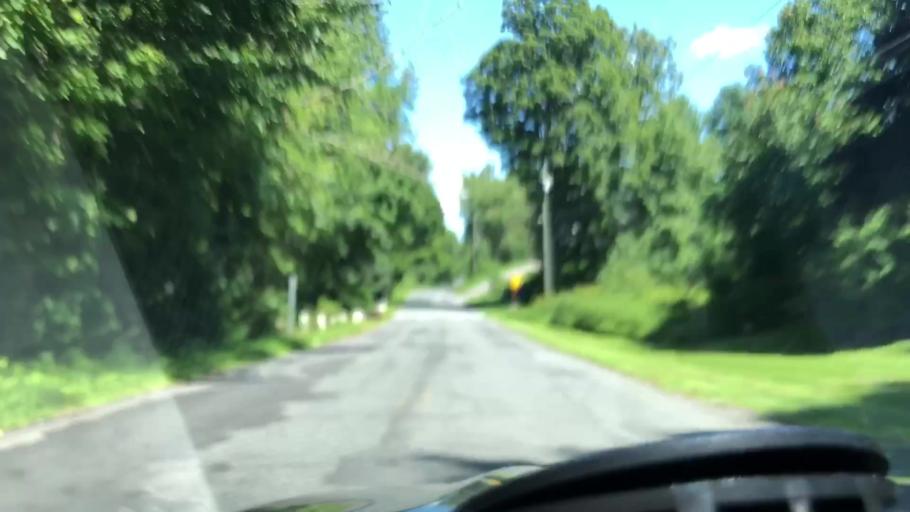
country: US
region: Massachusetts
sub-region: Berkshire County
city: Lanesborough
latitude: 42.5386
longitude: -73.2287
